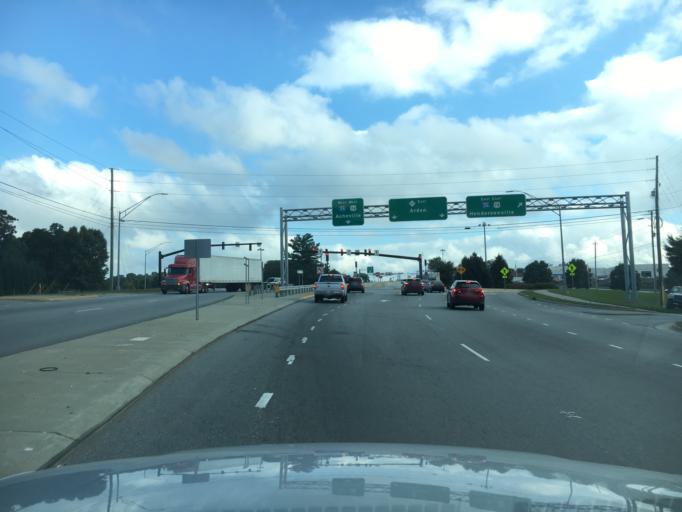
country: US
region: North Carolina
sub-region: Henderson County
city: Fletcher
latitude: 35.4384
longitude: -82.5365
